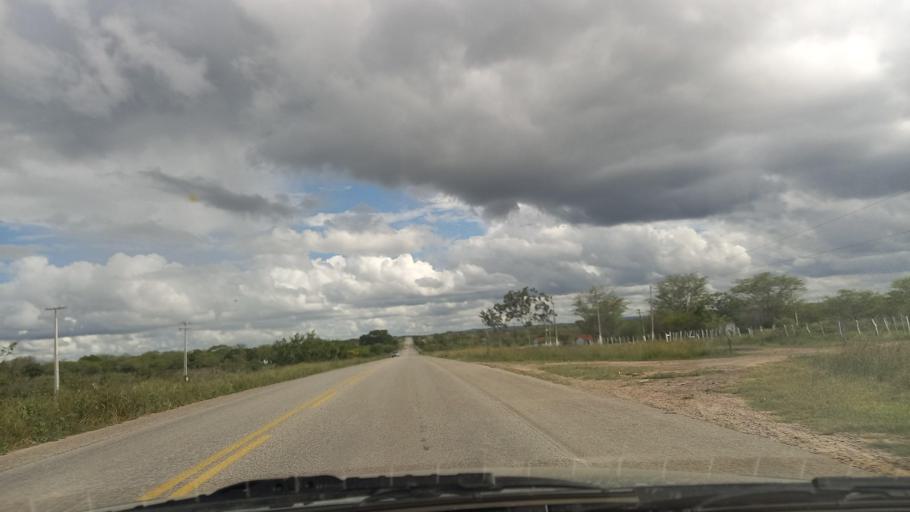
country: BR
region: Pernambuco
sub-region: Cachoeirinha
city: Cachoeirinha
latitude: -8.5094
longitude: -36.2513
